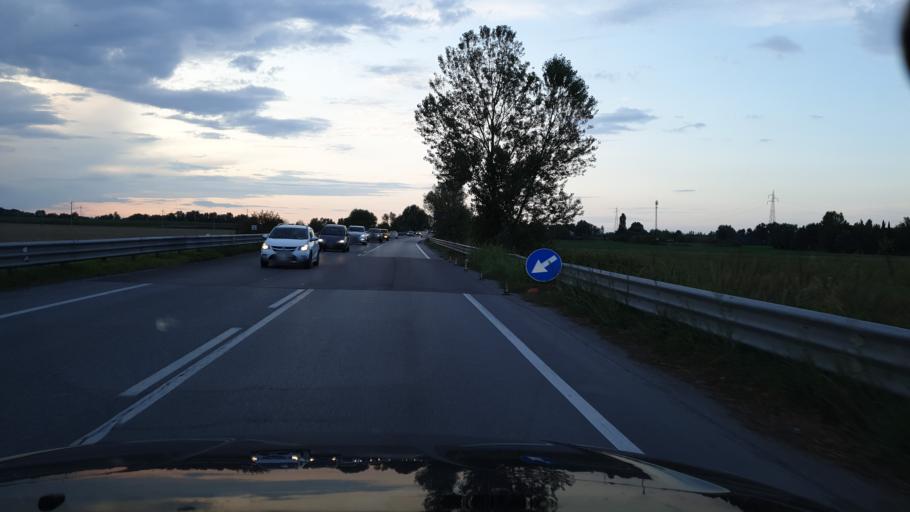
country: IT
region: Emilia-Romagna
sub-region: Provincia di Ravenna
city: Savio
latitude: 44.2970
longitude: 12.2952
